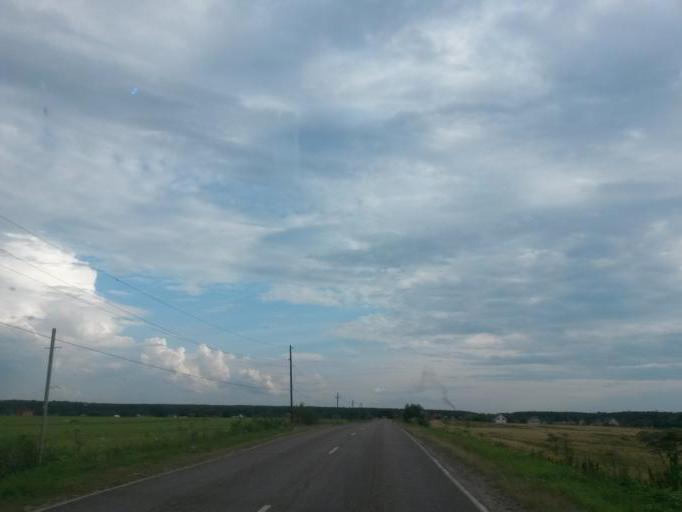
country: RU
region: Moskovskaya
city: Belyye Stolby
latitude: 55.2722
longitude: 37.7700
